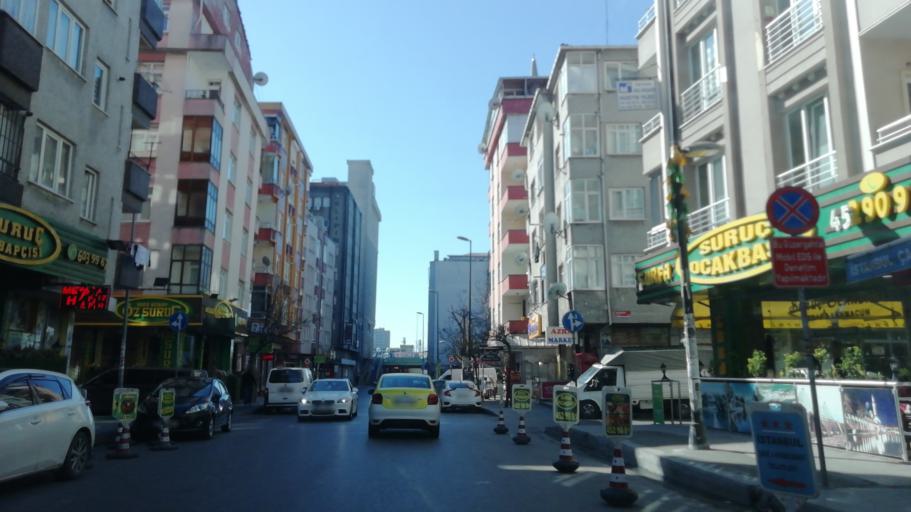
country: TR
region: Istanbul
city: Bahcelievler
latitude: 40.9937
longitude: 28.8387
